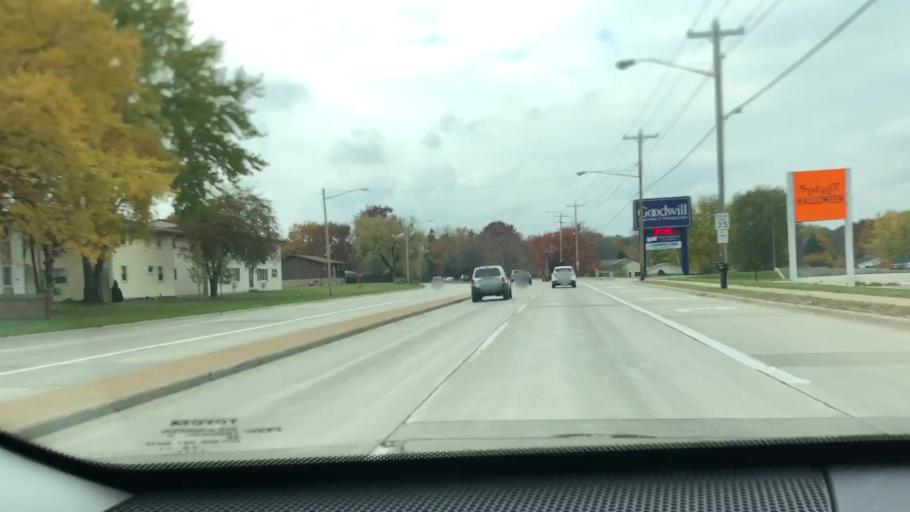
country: US
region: Wisconsin
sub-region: Brown County
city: Howard
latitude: 44.5246
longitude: -88.0666
